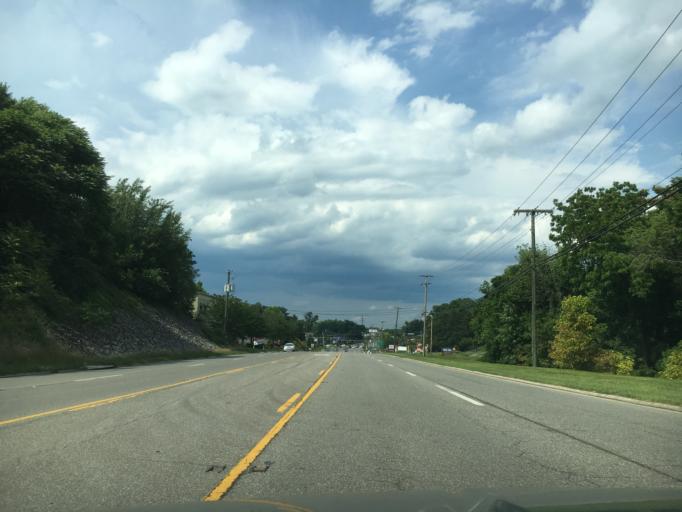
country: US
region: Virginia
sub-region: Roanoke County
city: Cave Spring
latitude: 37.2196
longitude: -80.0161
